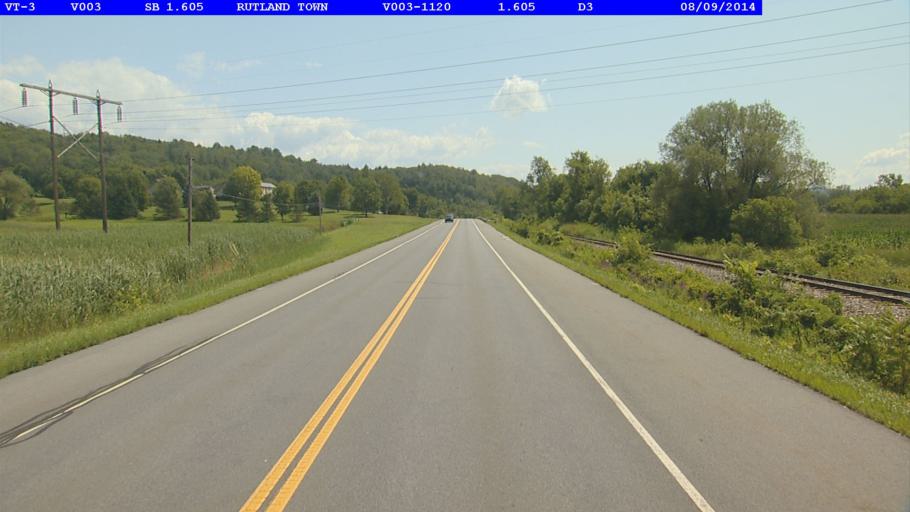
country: US
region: Vermont
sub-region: Rutland County
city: West Rutland
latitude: 43.6244
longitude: -73.0273
